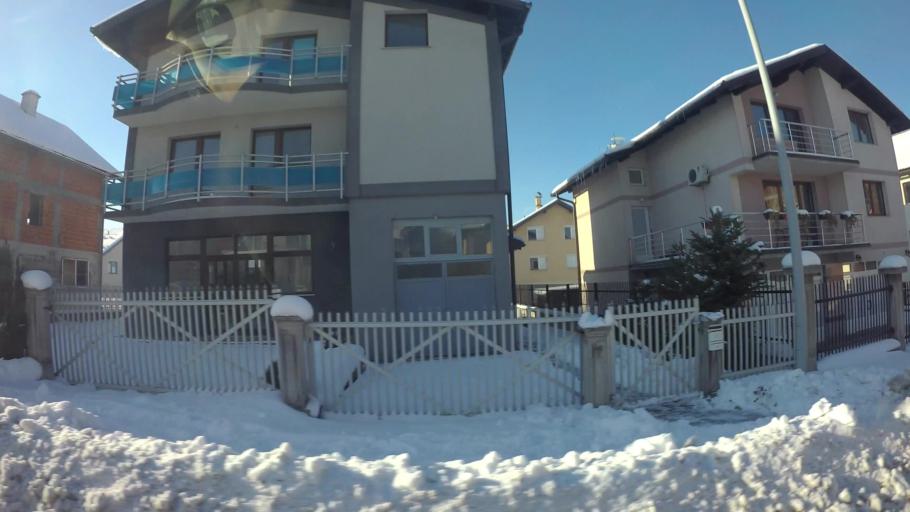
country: BA
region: Federation of Bosnia and Herzegovina
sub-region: Kanton Sarajevo
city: Sarajevo
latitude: 43.8208
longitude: 18.3689
